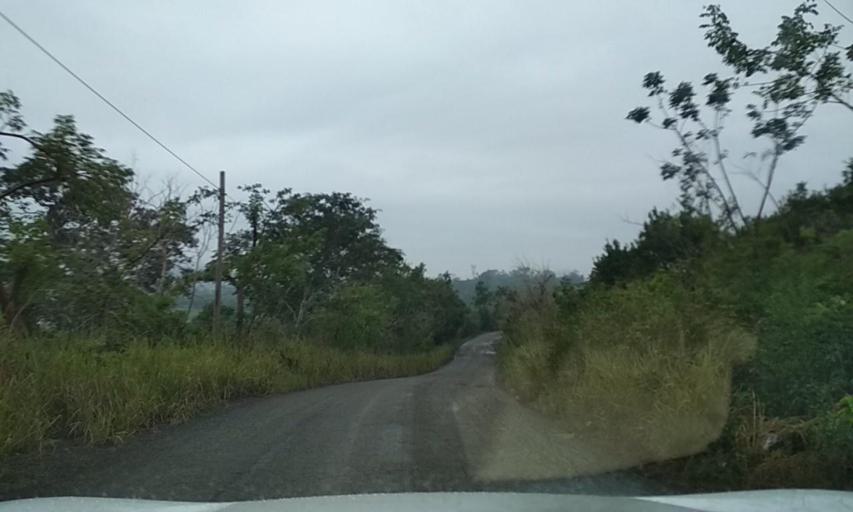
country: MX
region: Veracruz
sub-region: Coatzintla
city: Manuel Maria Contreras
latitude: 20.4648
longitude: -97.4713
